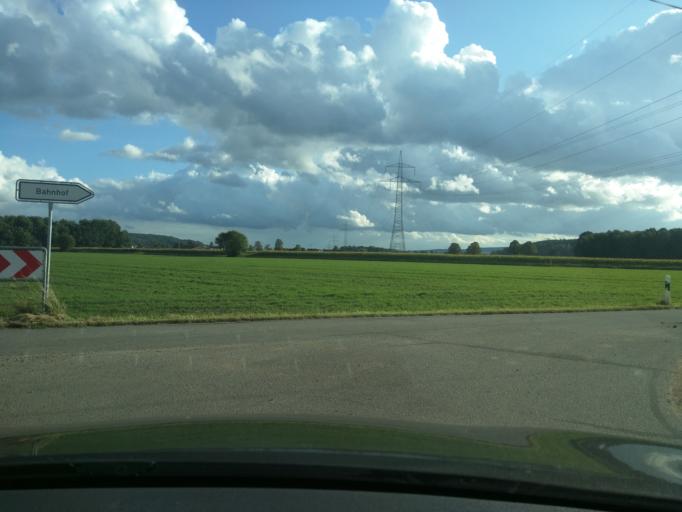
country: DE
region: Bavaria
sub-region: Upper Palatinate
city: Schwandorf in Bayern
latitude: 49.3623
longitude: 12.1062
